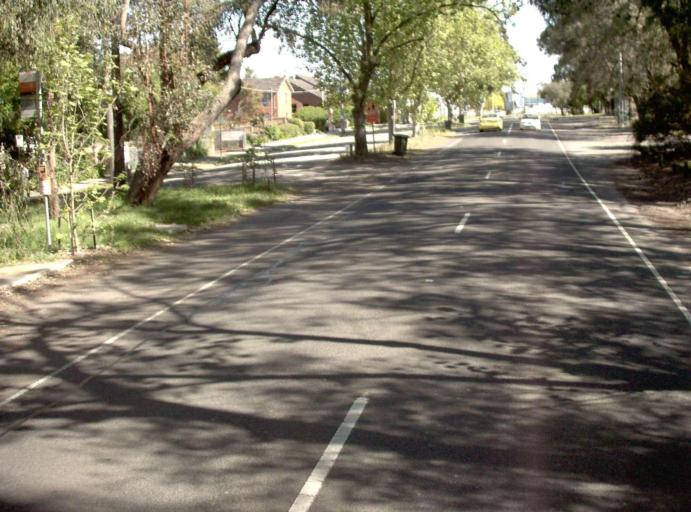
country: AU
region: Victoria
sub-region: Maroondah
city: Croydon North
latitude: -37.7924
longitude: 145.2819
